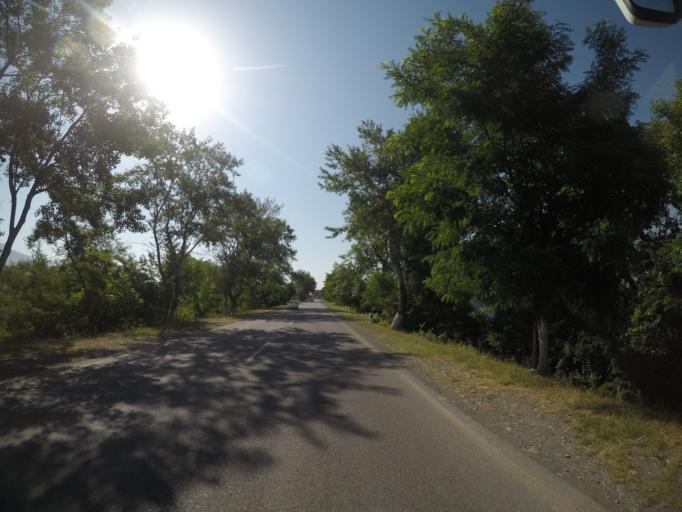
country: AZ
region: Oguz
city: Oguz
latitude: 41.0816
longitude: 47.2984
